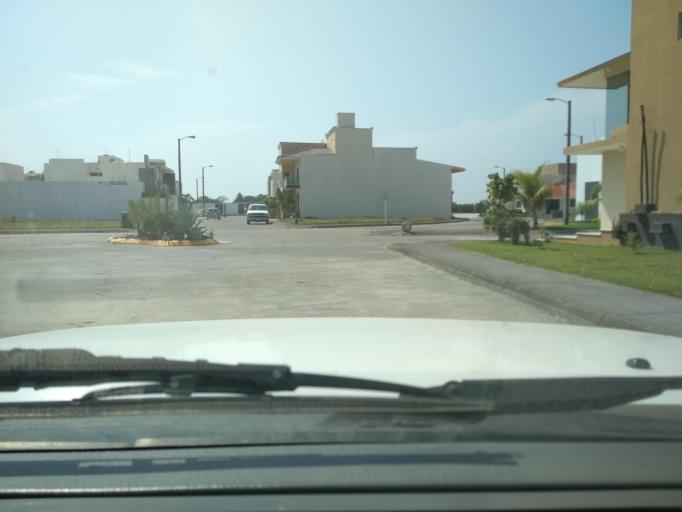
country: MX
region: Veracruz
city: Boca del Rio
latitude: 19.1046
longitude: -96.1248
